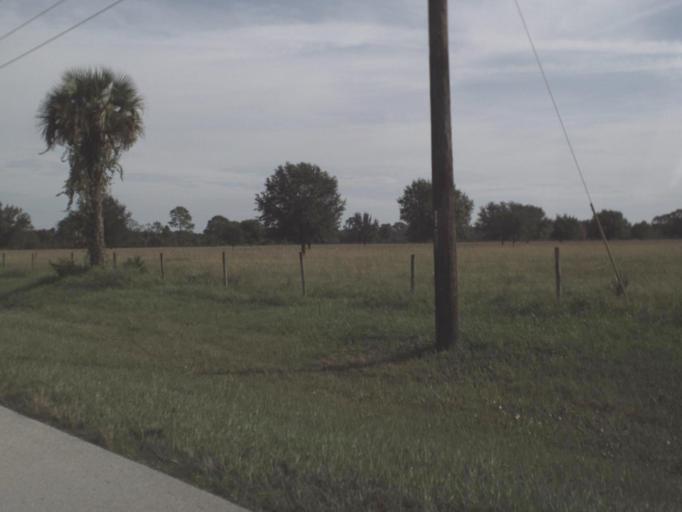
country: US
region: Florida
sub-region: Lee County
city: Fort Myers Shores
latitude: 26.7375
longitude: -81.7610
